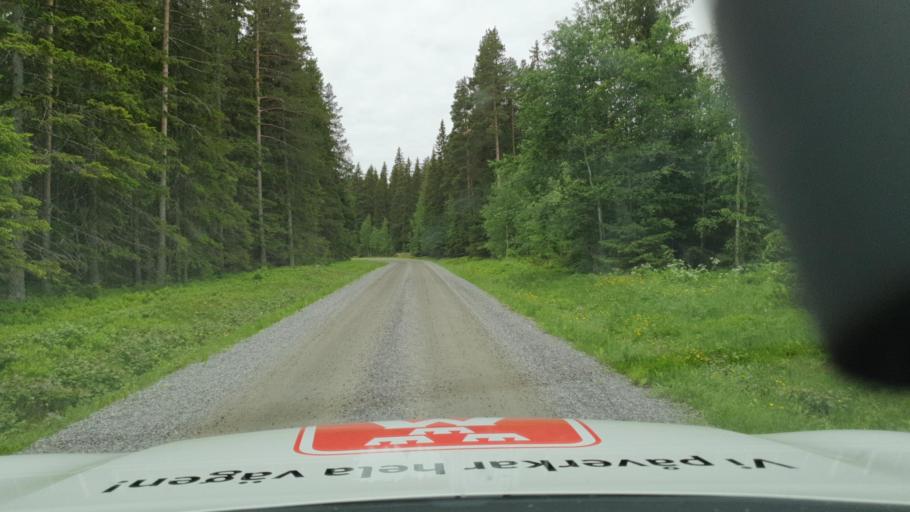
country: SE
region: Vaesterbotten
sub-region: Skelleftea Kommun
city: Burtraesk
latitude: 64.4489
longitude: 20.3882
